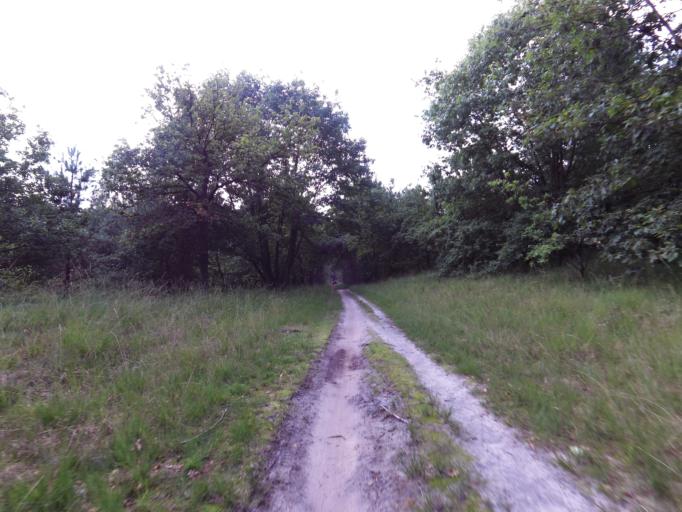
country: NL
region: North Brabant
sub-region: Gemeente Best
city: Best
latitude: 51.5064
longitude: 5.4285
